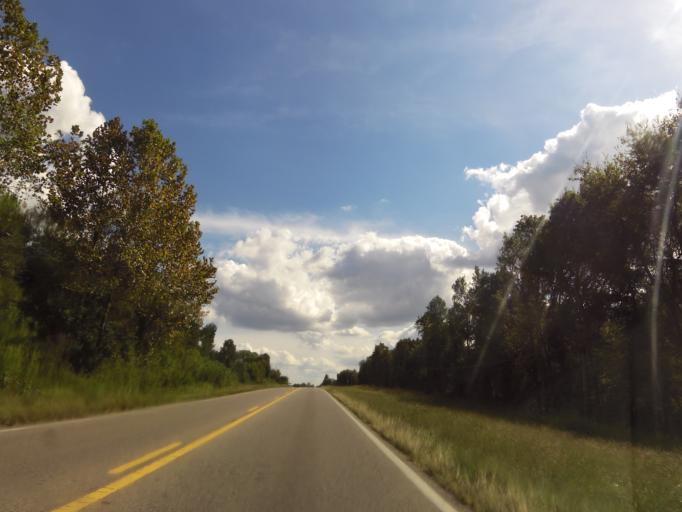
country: US
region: Alabama
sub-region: Dallas County
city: Selmont-West Selmont
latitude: 32.3451
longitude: -86.9987
